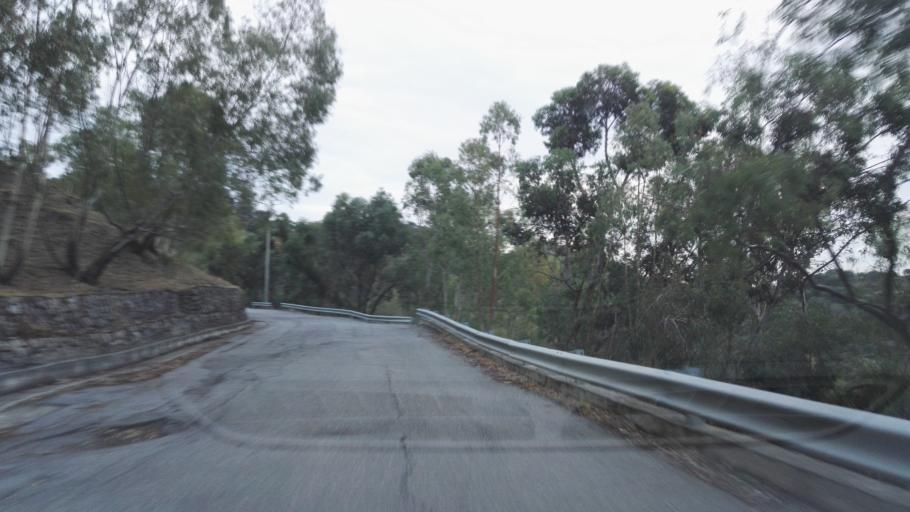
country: IT
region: Calabria
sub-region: Provincia di Reggio Calabria
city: Caulonia
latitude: 38.3866
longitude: 16.4010
